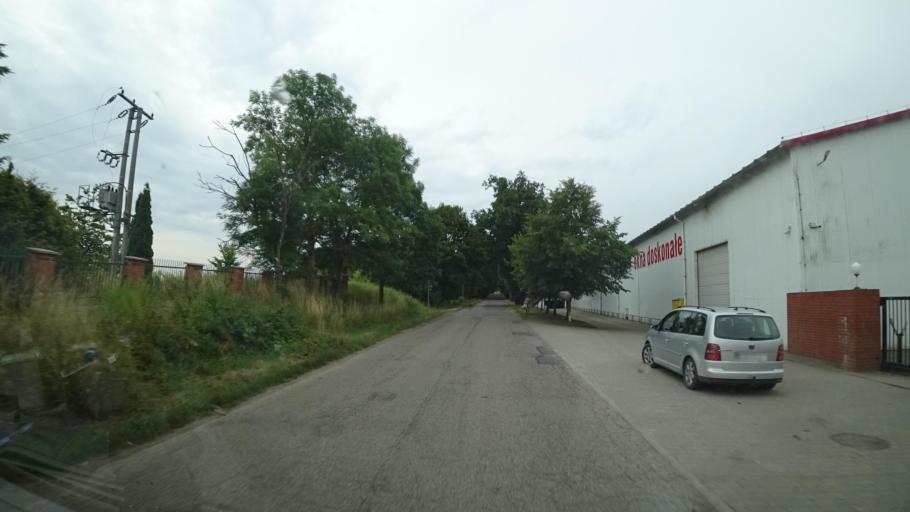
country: PL
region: Warmian-Masurian Voivodeship
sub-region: Powiat gizycki
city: Ryn
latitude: 53.9329
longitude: 21.5497
